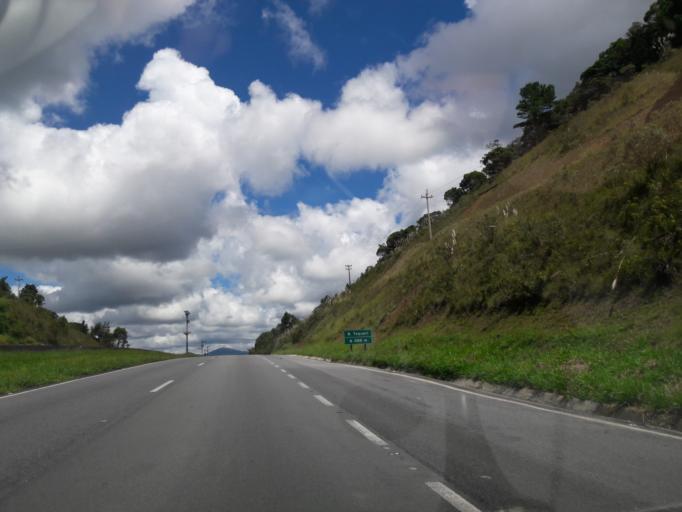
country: BR
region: Parana
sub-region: Campina Grande Do Sul
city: Campina Grande do Sul
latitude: -25.2701
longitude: -48.9193
